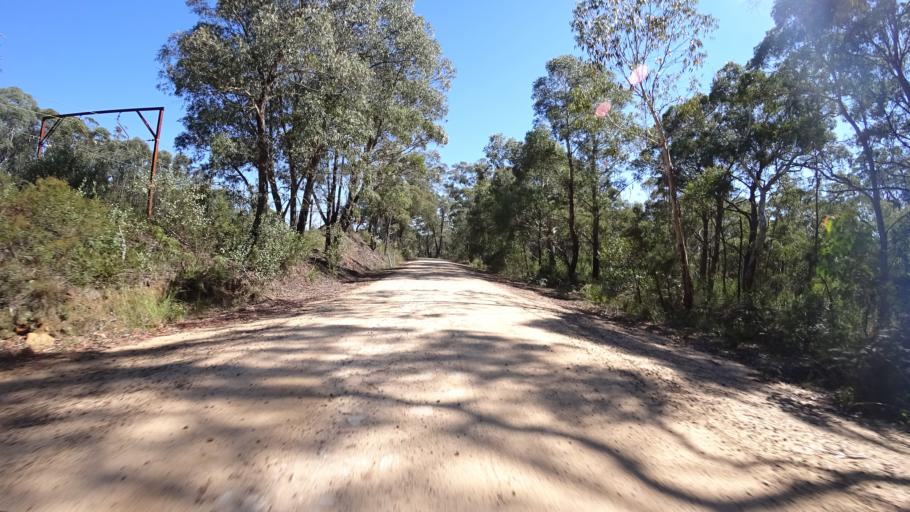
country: AU
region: New South Wales
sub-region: Lithgow
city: Lithgow
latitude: -33.4803
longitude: 150.2541
